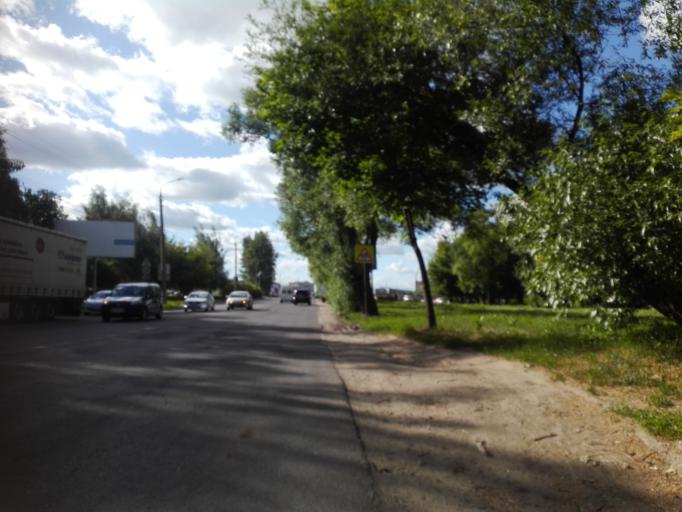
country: RU
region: Orjol
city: Orel
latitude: 52.9365
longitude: 36.0357
